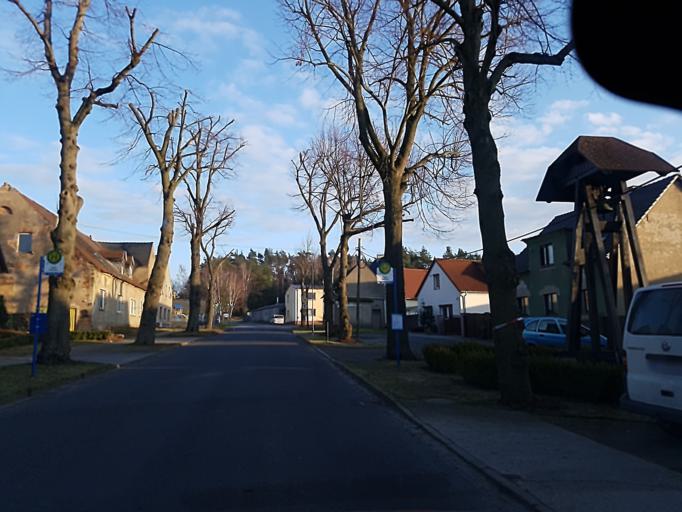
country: DE
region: Brandenburg
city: Schonborn
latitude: 51.5417
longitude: 13.4754
